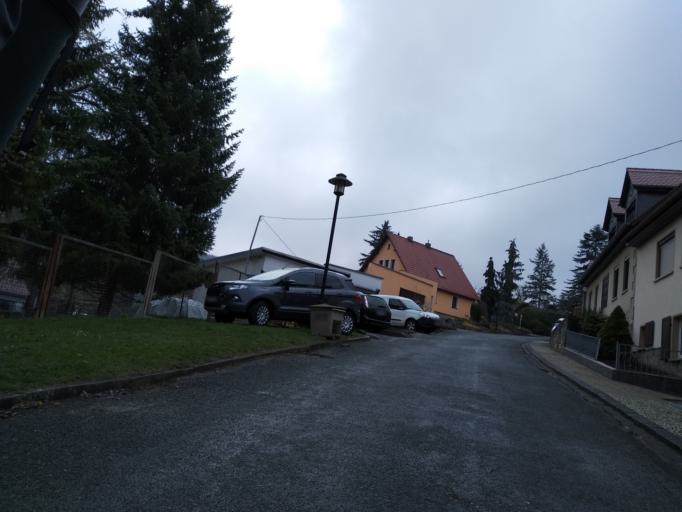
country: DE
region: Thuringia
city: Buchfart
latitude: 50.9197
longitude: 11.3323
